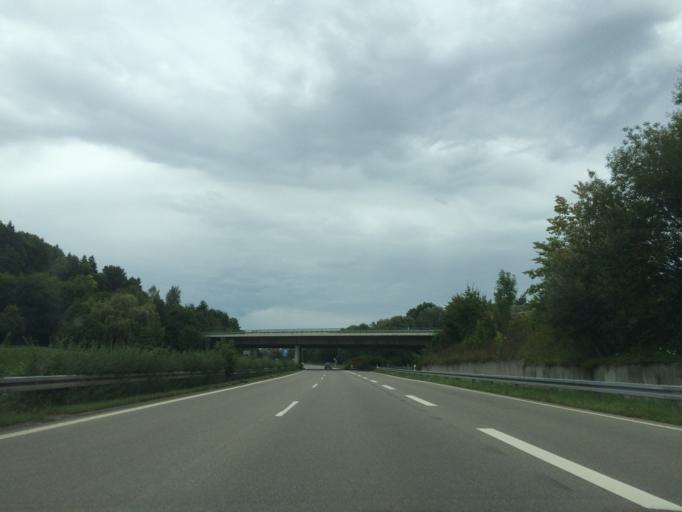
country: DE
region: Baden-Wuerttemberg
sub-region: Tuebingen Region
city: Ravensburg
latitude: 47.7970
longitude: 9.6066
